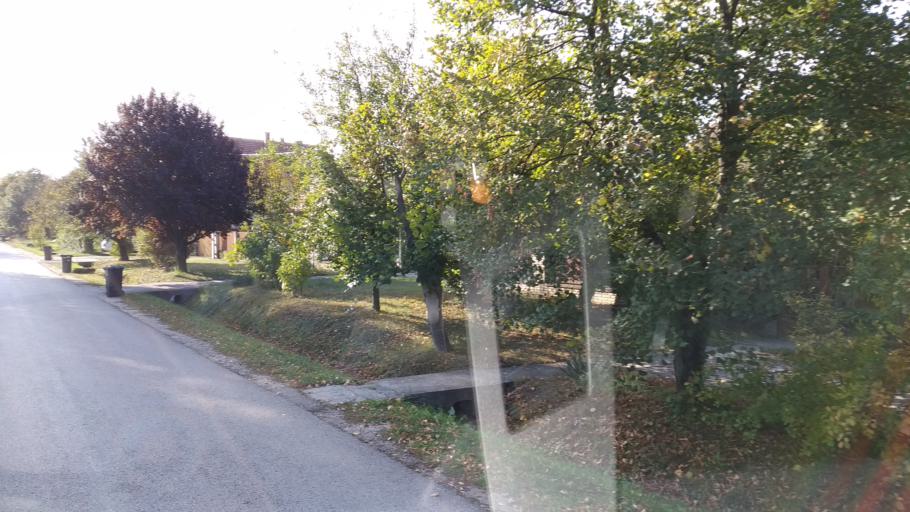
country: HU
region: Pest
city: Budakalasz
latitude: 47.6190
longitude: 19.0364
